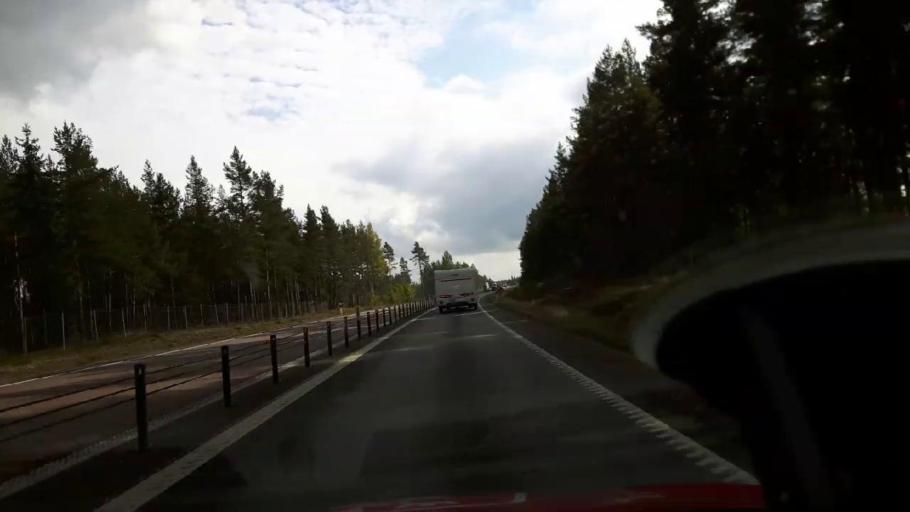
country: SE
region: Gaevleborg
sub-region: Gavle Kommun
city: Norrsundet
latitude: 60.9884
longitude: 17.0084
